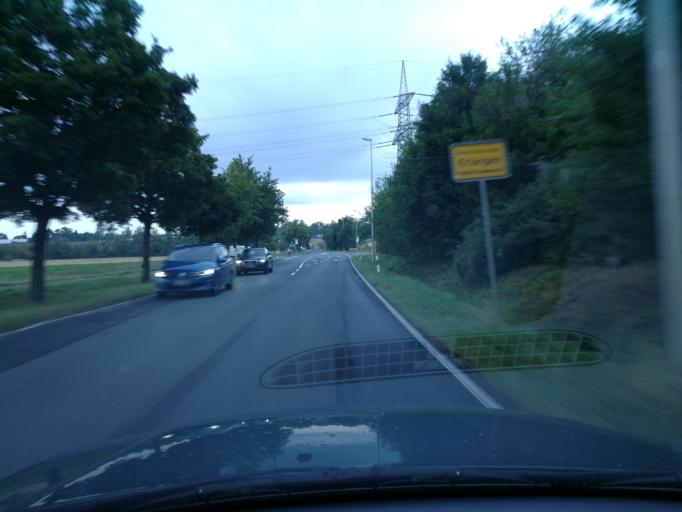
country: DE
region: Bavaria
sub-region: Regierungsbezirk Mittelfranken
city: Erlangen
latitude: 49.5584
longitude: 10.9616
